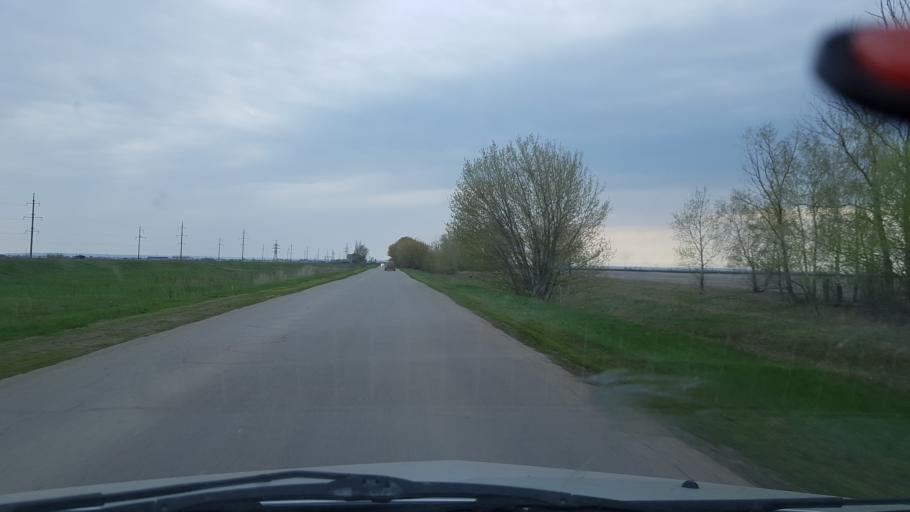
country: RU
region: Samara
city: Khryashchevka
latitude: 53.6700
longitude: 49.1177
